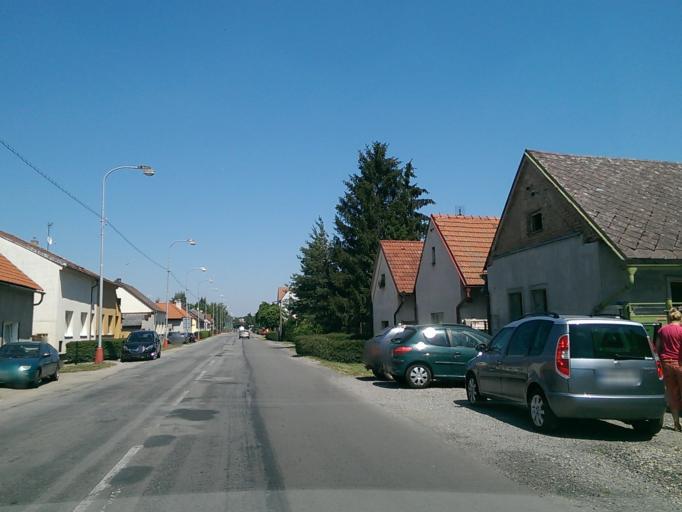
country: CZ
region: Central Bohemia
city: Benatky nad Jizerou
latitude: 50.2879
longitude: 14.8346
